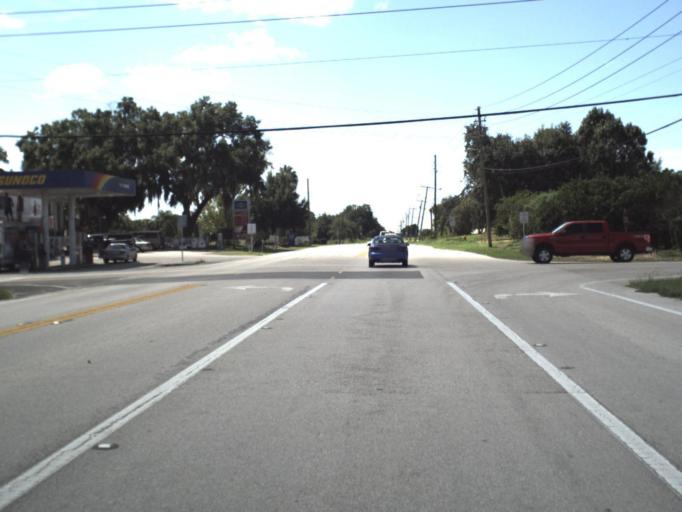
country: US
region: Florida
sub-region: Polk County
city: Lake Hamilton
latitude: 28.0558
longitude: -81.6199
